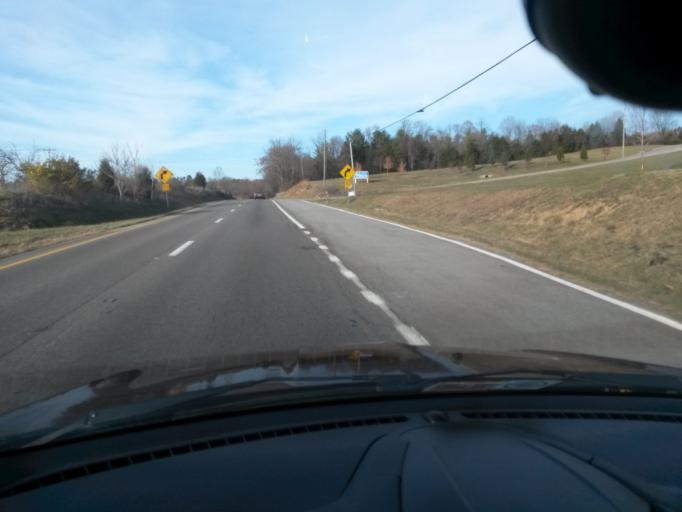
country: US
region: Virginia
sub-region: Botetourt County
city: Daleville
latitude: 37.4415
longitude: -79.9040
